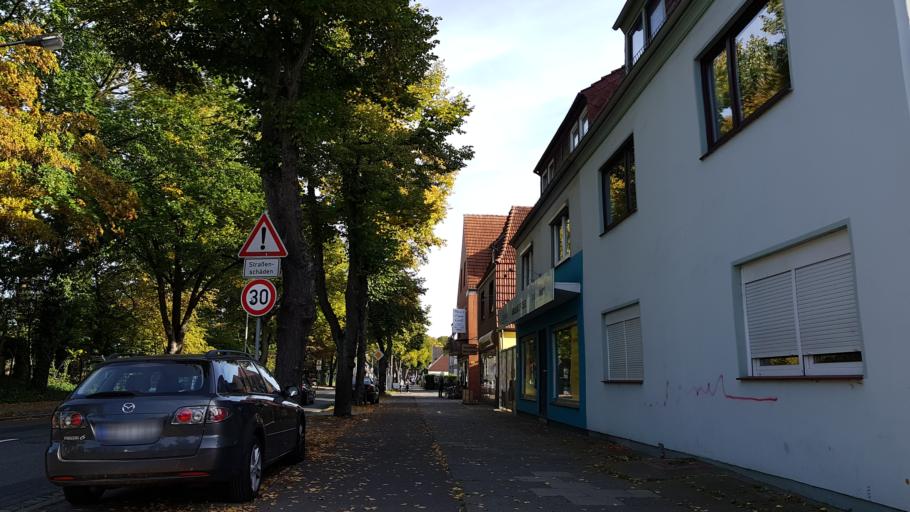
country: DE
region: Lower Saxony
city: Lilienthal
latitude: 53.0451
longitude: 8.8961
